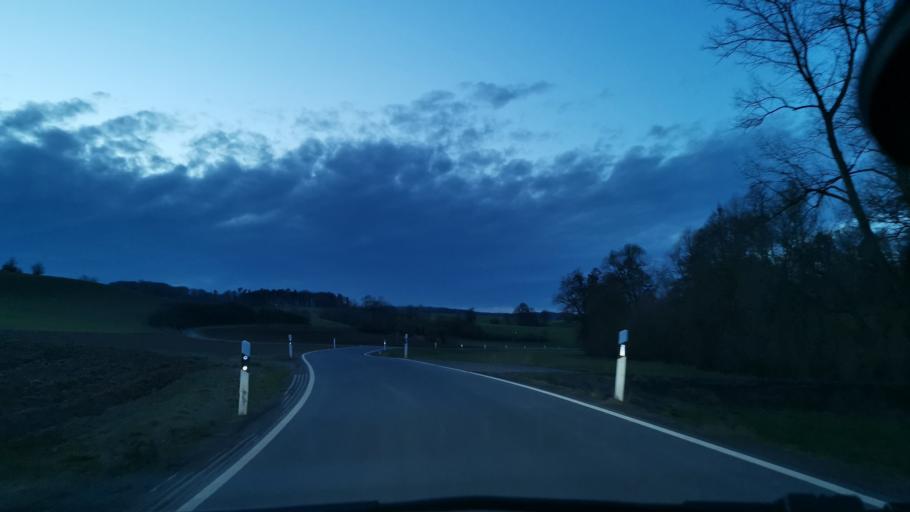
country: DE
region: Hesse
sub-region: Regierungsbezirk Kassel
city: Cornberg
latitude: 51.0566
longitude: 9.8352
